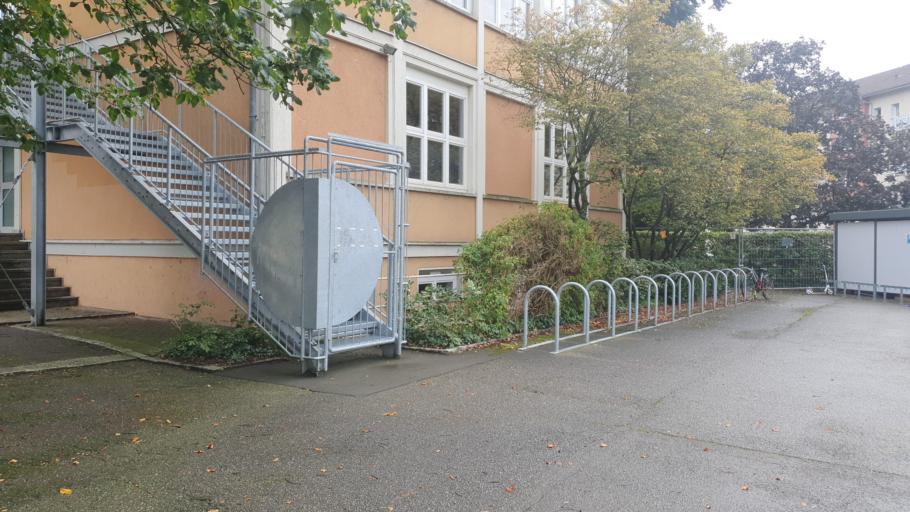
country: DE
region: Baden-Wuerttemberg
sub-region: Freiburg Region
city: Weil am Rhein
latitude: 47.5905
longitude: 7.6265
